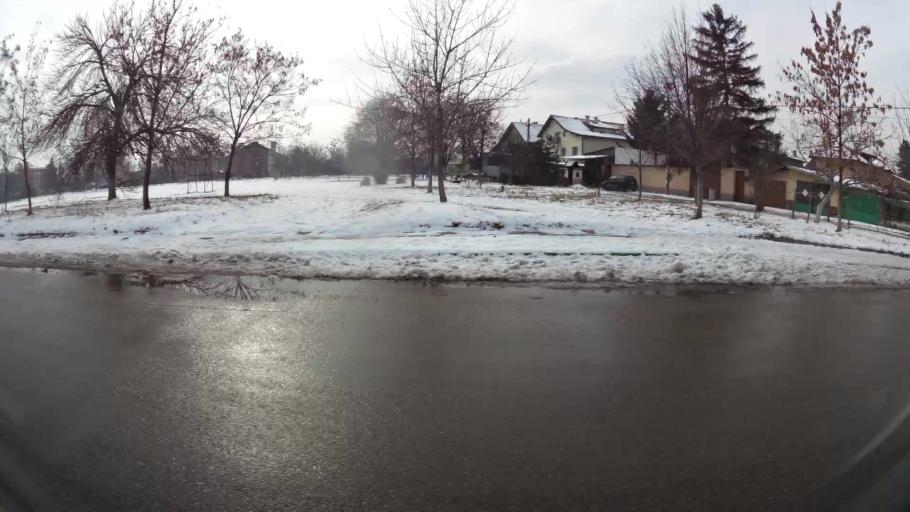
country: BG
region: Sofia-Capital
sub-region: Stolichna Obshtina
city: Sofia
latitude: 42.7120
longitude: 23.4069
